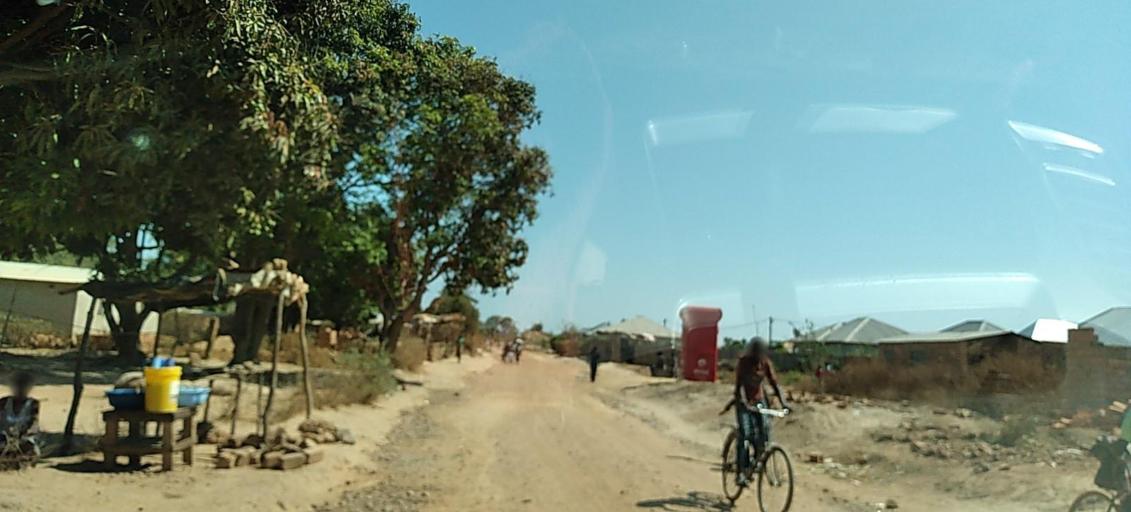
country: ZM
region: Copperbelt
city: Chililabombwe
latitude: -12.3255
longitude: 27.8603
